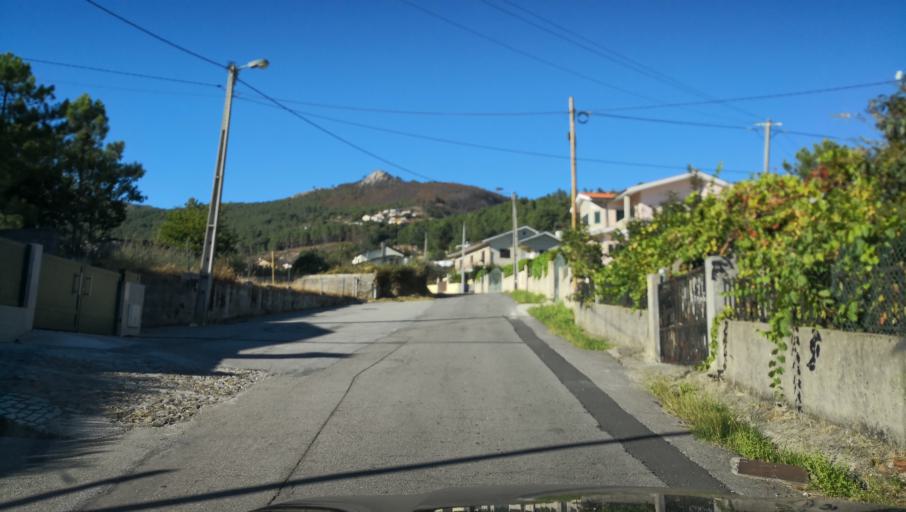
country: PT
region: Vila Real
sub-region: Vila Real
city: Vila Real
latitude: 41.3242
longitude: -7.7690
